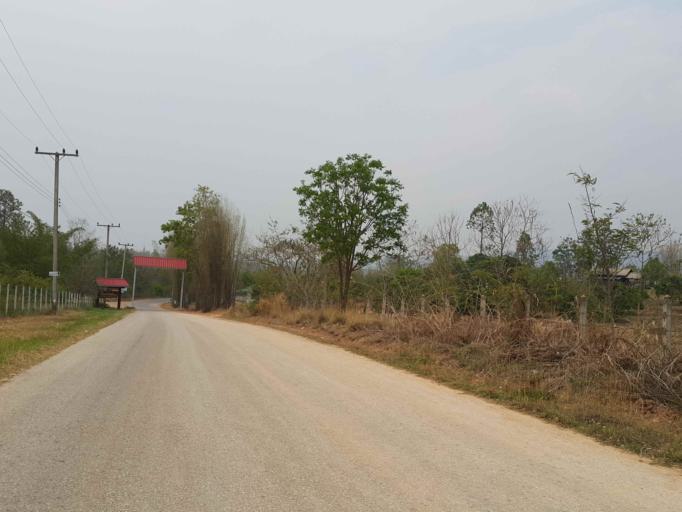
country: TH
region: Chiang Mai
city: San Sai
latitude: 18.9350
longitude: 99.0128
